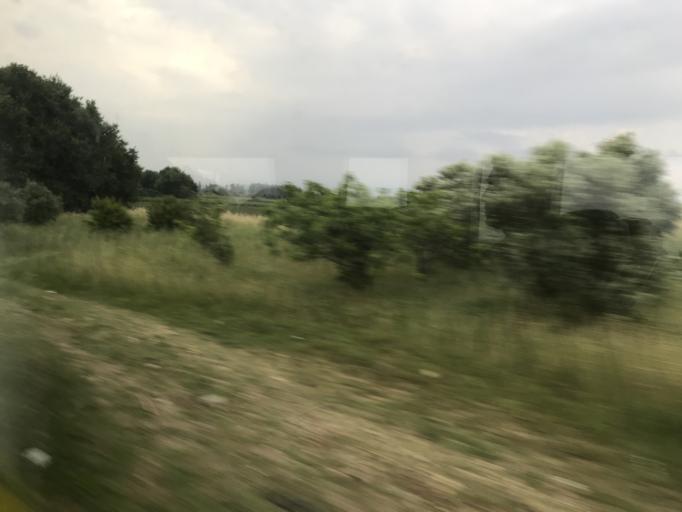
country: GR
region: East Macedonia and Thrace
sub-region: Nomos Rodopis
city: Arisvi
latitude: 41.0768
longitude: 25.5774
